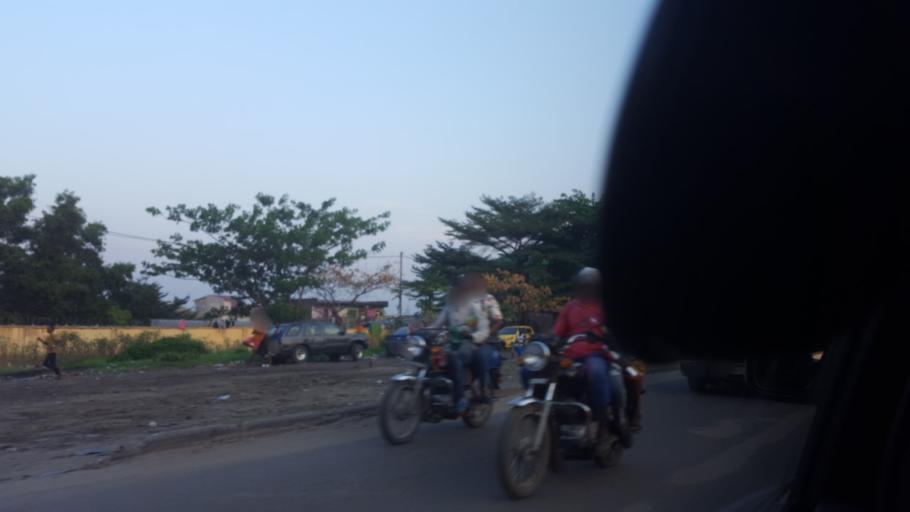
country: CD
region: Kinshasa
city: Kinshasa
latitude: -4.3473
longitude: 15.3249
